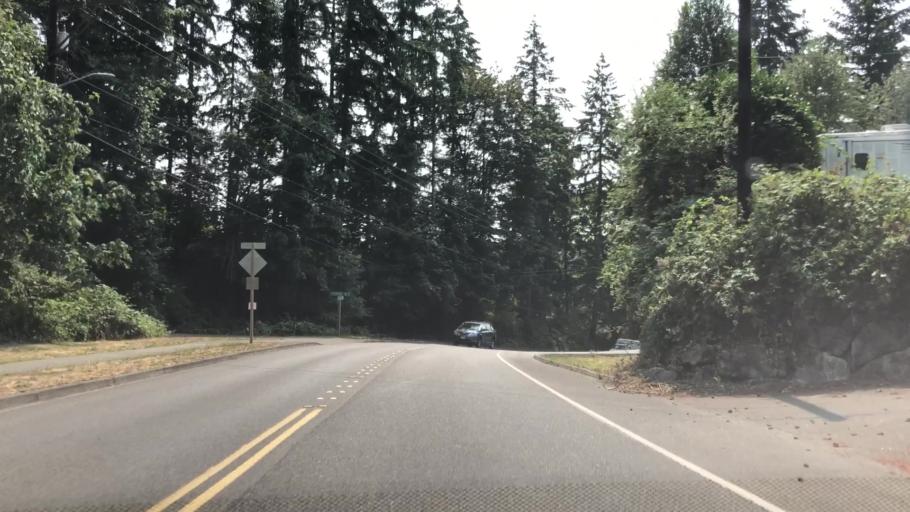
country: US
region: Washington
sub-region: Snohomish County
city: Alderwood Manor
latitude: 47.8100
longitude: -122.2497
